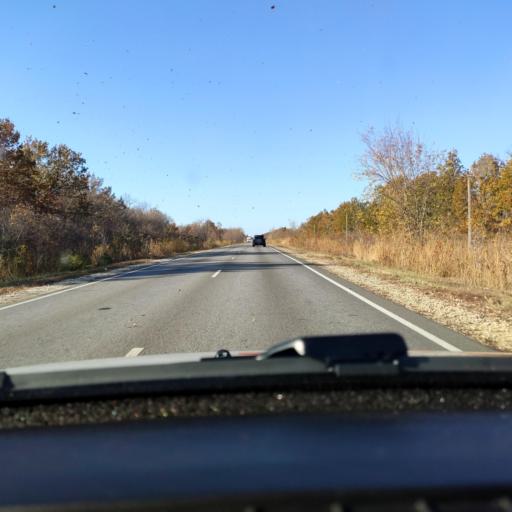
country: RU
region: Voronezj
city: Zemlyansk
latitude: 51.8224
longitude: 38.8383
